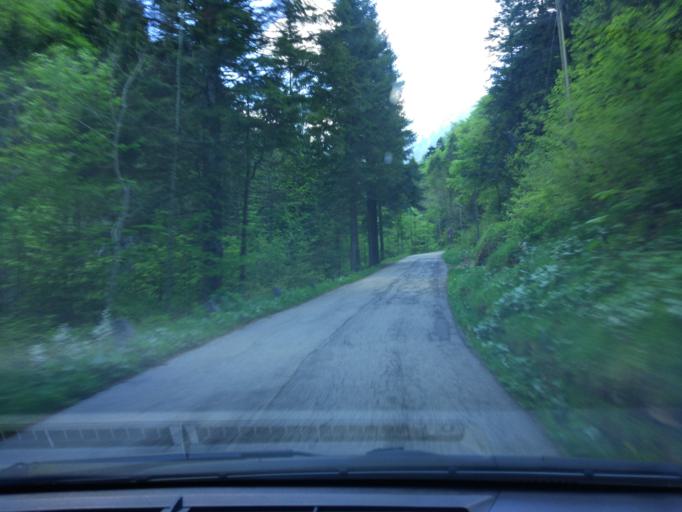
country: IT
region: Veneto
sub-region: Provincia di Verona
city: Selva di Progno
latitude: 45.6802
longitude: 11.1162
